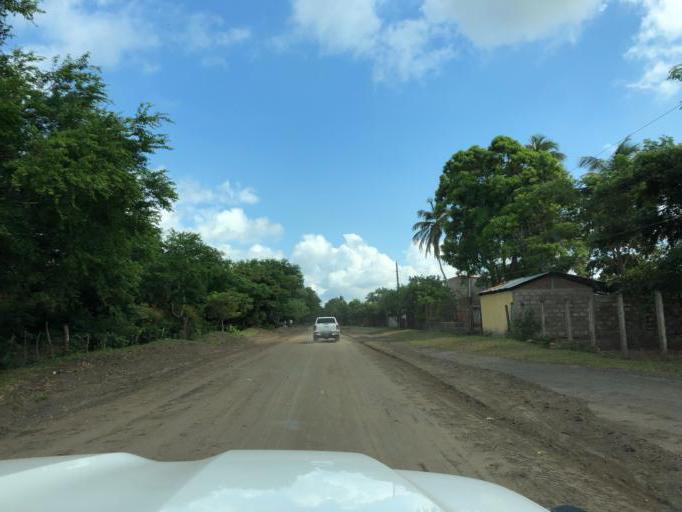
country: NI
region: Granada
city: Granada
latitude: 11.9989
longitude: -85.9358
